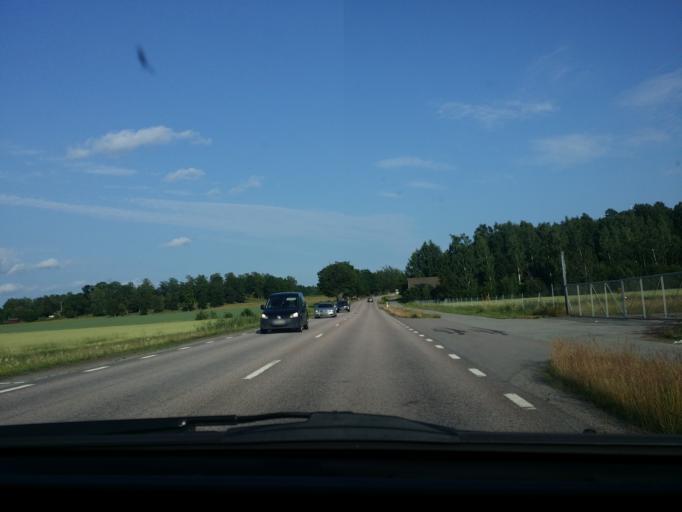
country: SE
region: Vaestmanland
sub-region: Vasteras
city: Tillberga
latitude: 59.6072
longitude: 16.6434
